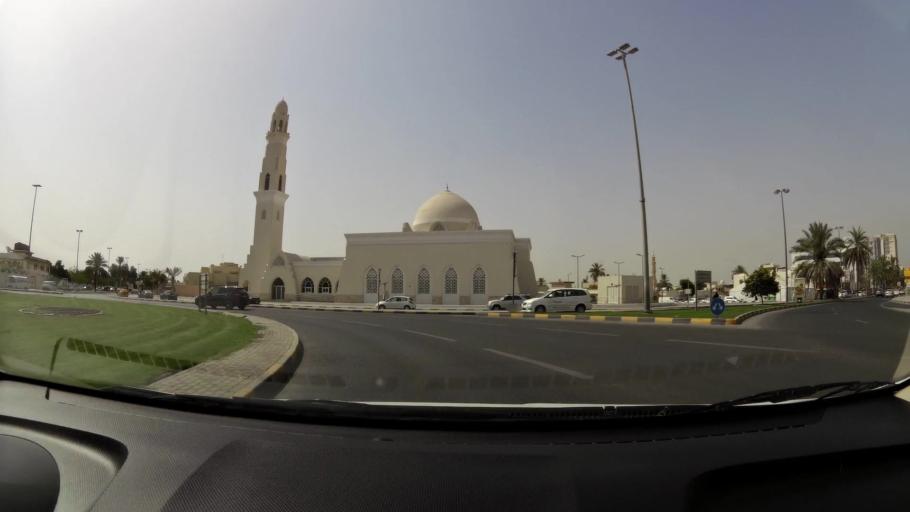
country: AE
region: Ash Shariqah
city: Sharjah
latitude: 25.3732
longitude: 55.4075
